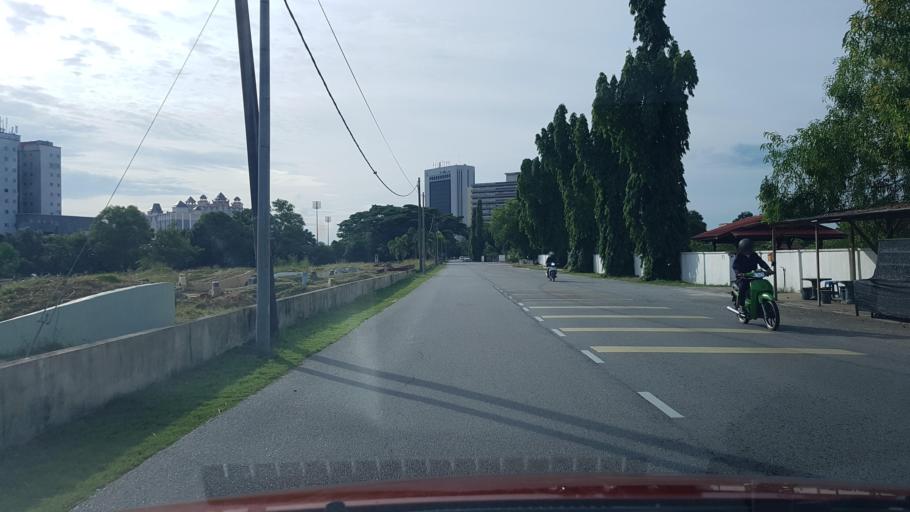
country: MY
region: Terengganu
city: Kuala Terengganu
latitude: 5.3248
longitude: 103.1442
